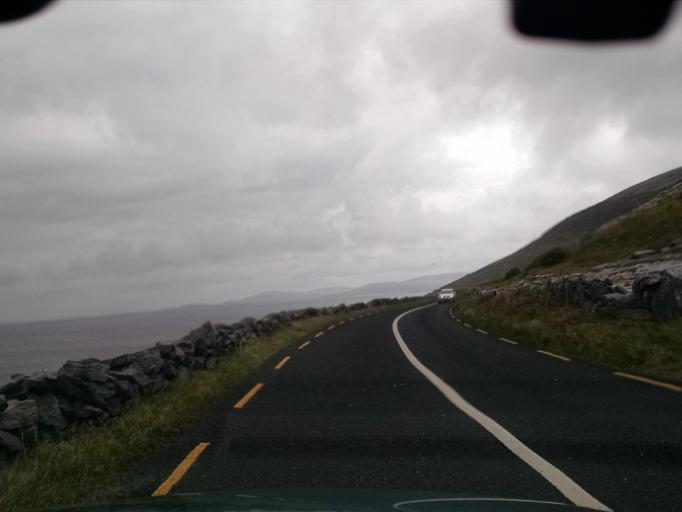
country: IE
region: Connaught
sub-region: County Galway
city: Bearna
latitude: 53.1537
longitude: -9.2627
